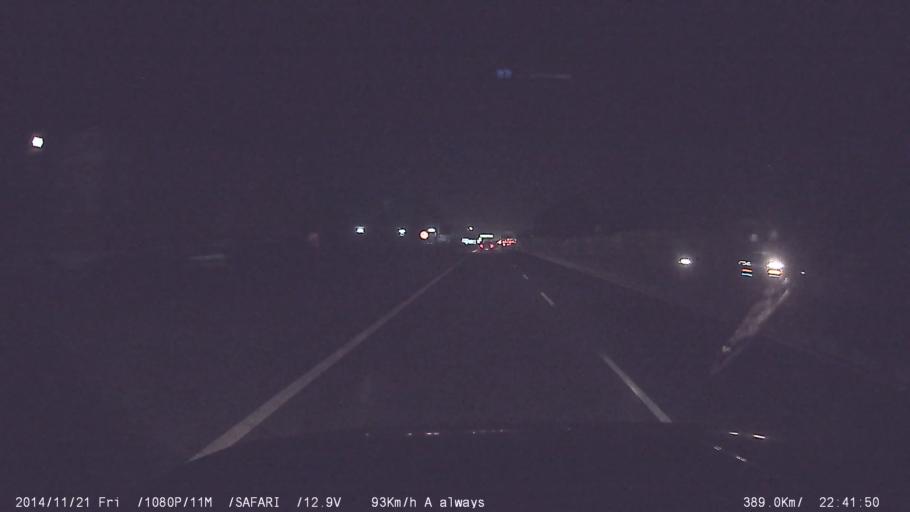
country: IN
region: Tamil Nadu
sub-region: Villupuram
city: Tindivanam
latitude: 12.2451
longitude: 79.6674
